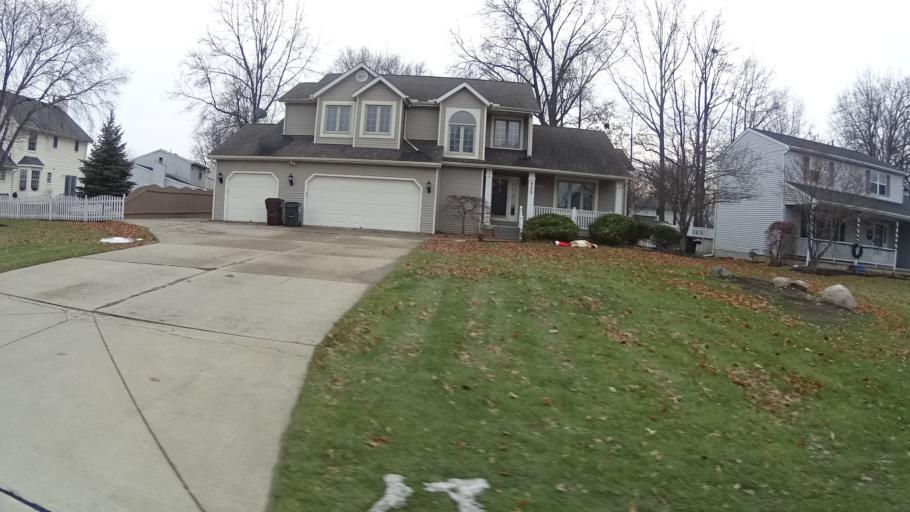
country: US
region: Ohio
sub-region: Lorain County
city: Amherst
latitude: 41.3985
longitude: -82.1931
